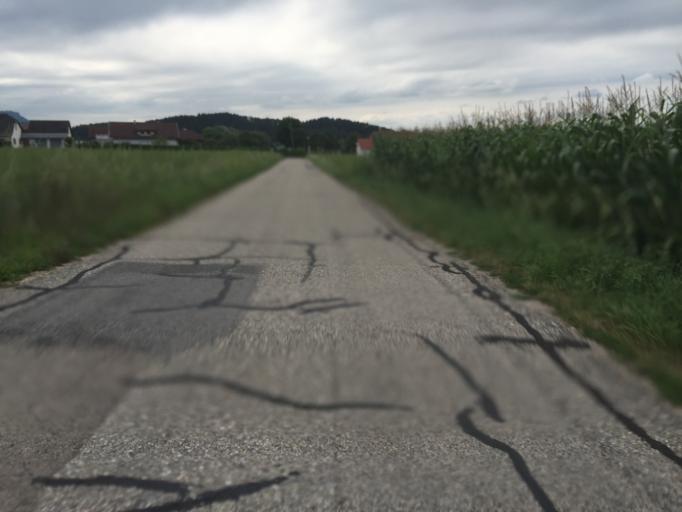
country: AT
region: Carinthia
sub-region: Politischer Bezirk Volkermarkt
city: Feistritz ob Bleiburg
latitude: 46.5584
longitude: 14.7691
